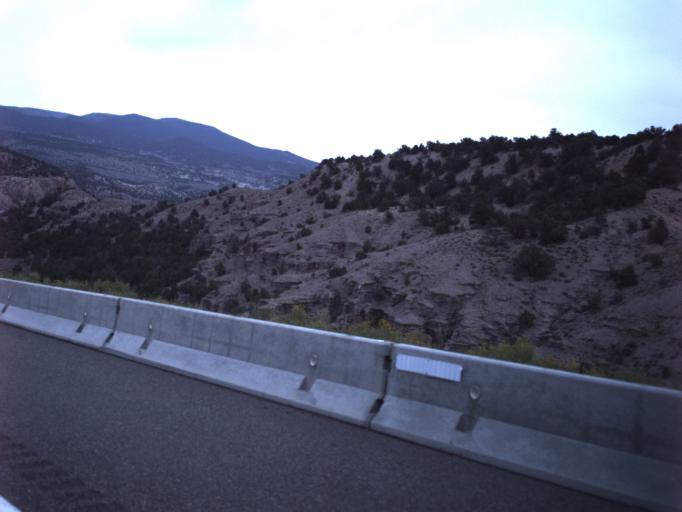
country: US
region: Utah
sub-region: Sevier County
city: Monroe
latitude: 38.5562
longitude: -112.3628
